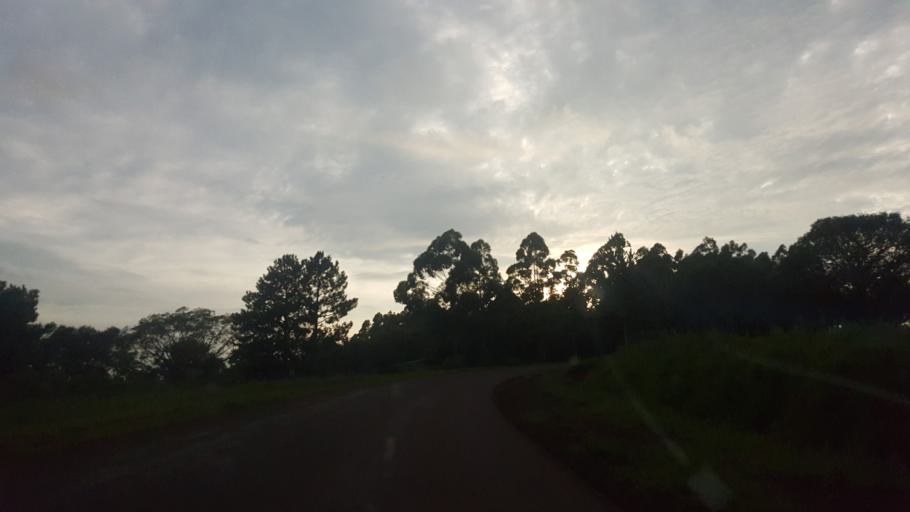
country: AR
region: Misiones
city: Dos de Mayo
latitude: -27.0038
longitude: -54.6949
